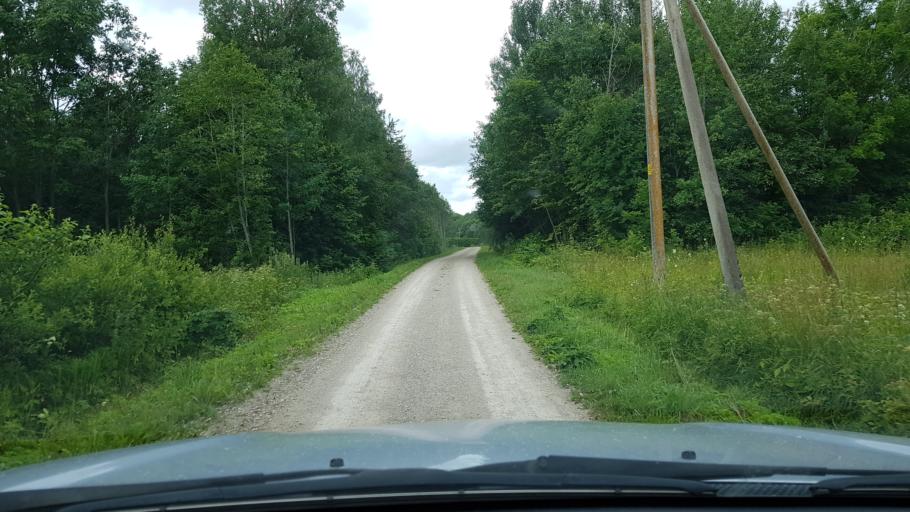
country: EE
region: Ida-Virumaa
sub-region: Narva-Joesuu linn
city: Narva-Joesuu
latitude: 59.4072
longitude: 27.9795
